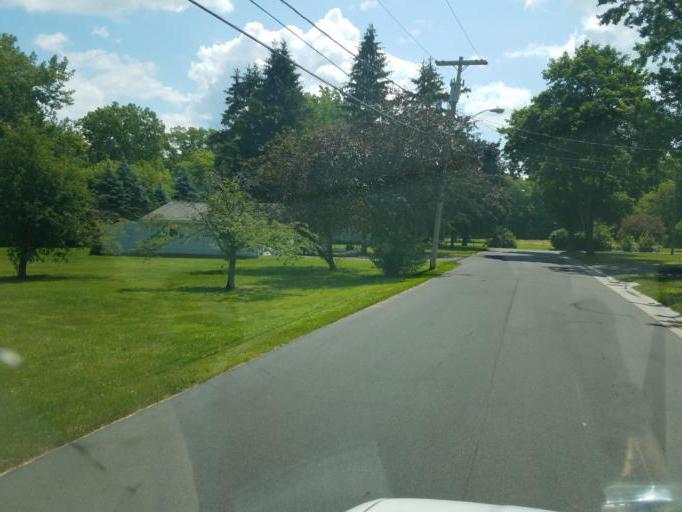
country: US
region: New York
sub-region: Wayne County
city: Clyde
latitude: 43.0774
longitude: -76.8660
